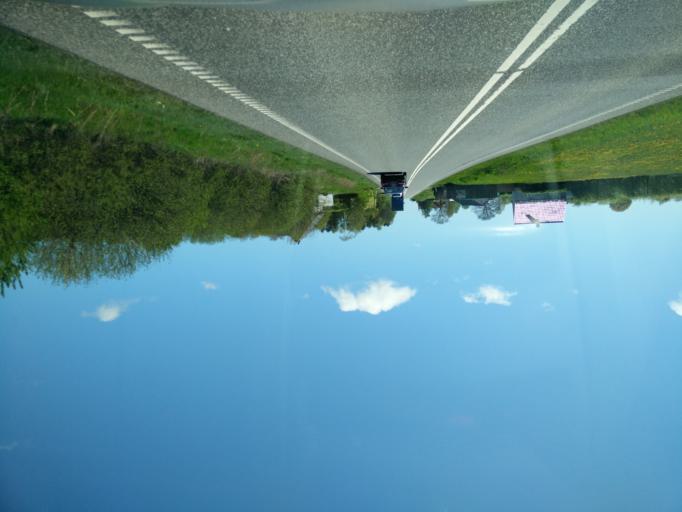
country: DK
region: Capital Region
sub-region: Gribskov Kommune
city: Helsinge
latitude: 56.0074
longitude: 12.2304
